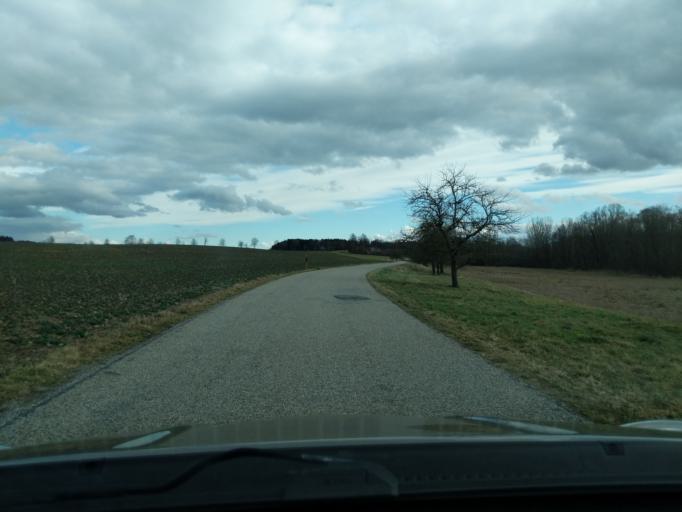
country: DE
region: Bavaria
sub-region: Upper Bavaria
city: Kirchseeon
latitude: 48.0688
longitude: 11.9120
